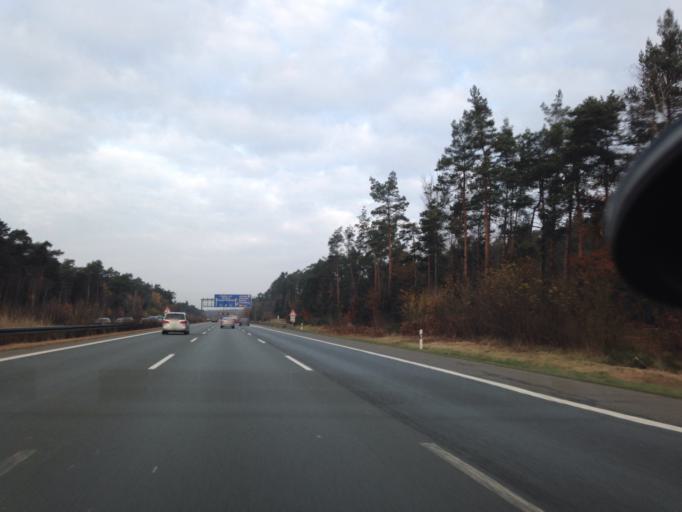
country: DE
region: Bavaria
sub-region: Regierungsbezirk Mittelfranken
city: Heroldsberg
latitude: 49.4916
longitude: 11.1523
